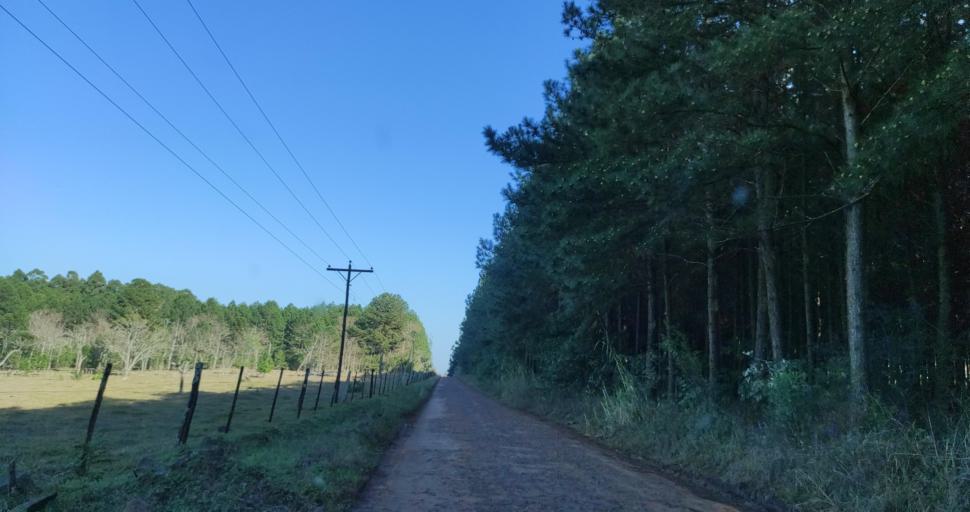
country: AR
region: Misiones
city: Puerto Rico
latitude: -26.8618
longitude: -55.0175
